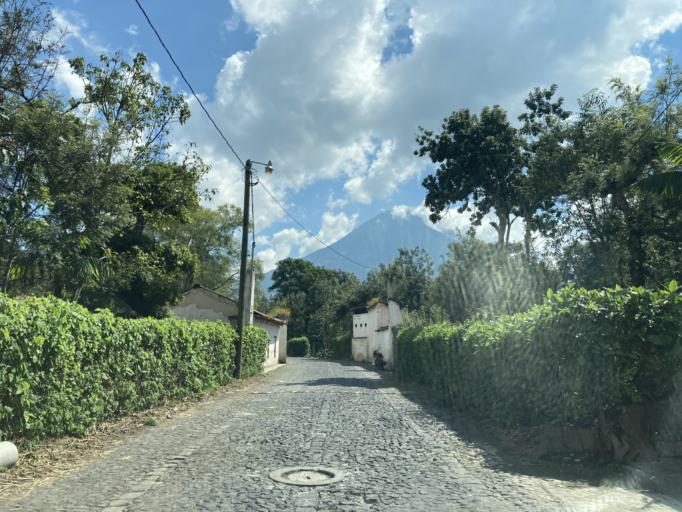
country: GT
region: Sacatepequez
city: Antigua Guatemala
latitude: 14.5491
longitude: -90.7332
